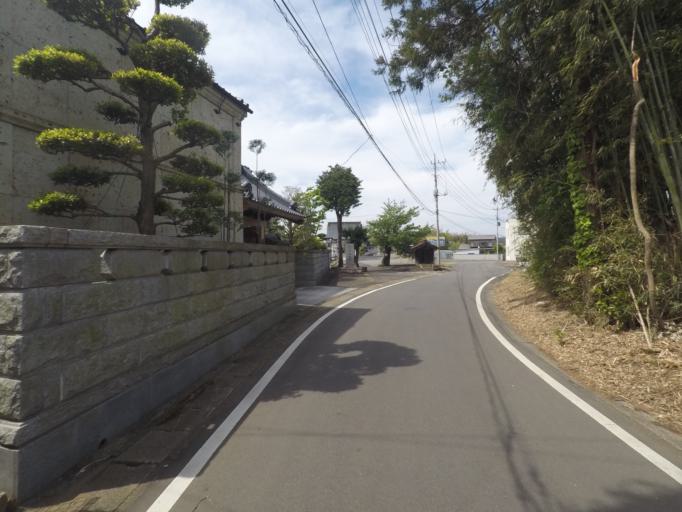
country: JP
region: Ibaraki
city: Ishige
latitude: 36.1398
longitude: 140.0232
